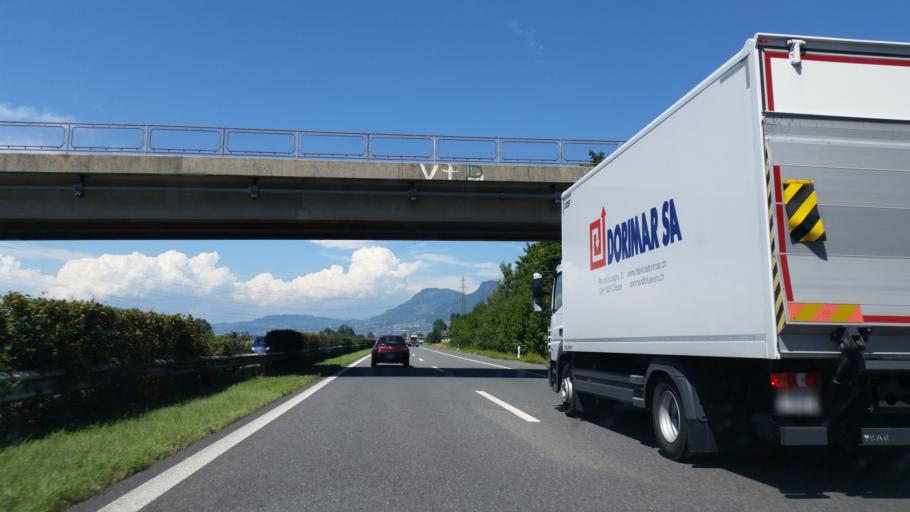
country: CH
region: Vaud
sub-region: Aigle District
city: Villeneuve
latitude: 46.3626
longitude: 6.9232
